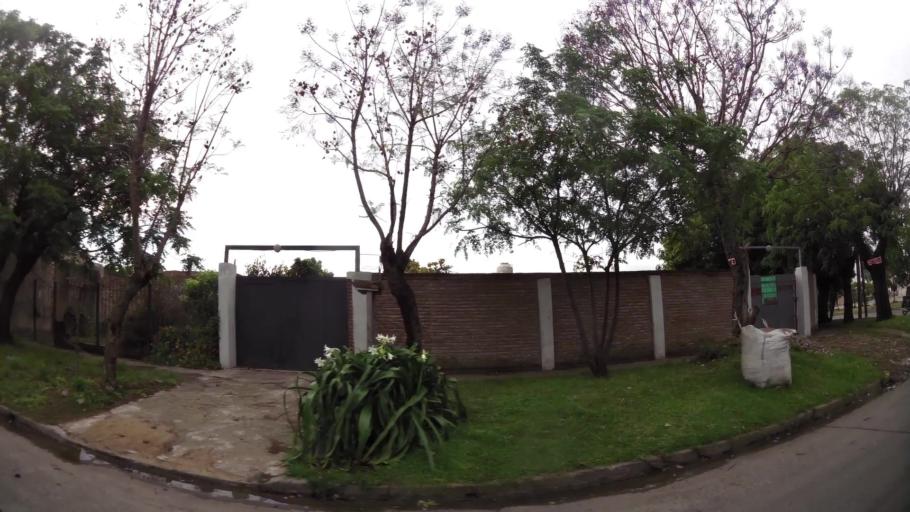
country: AR
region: Buenos Aires
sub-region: Partido de Lomas de Zamora
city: Lomas de Zamora
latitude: -34.7429
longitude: -58.3436
